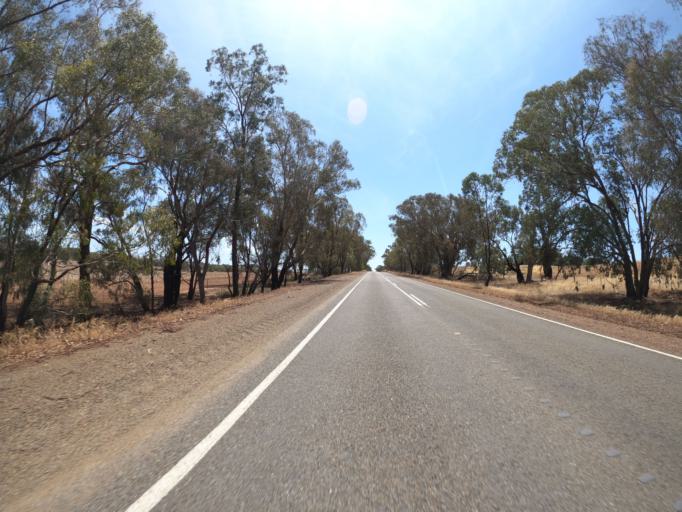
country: AU
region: Victoria
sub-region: Benalla
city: Benalla
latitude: -36.3517
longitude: 145.9633
